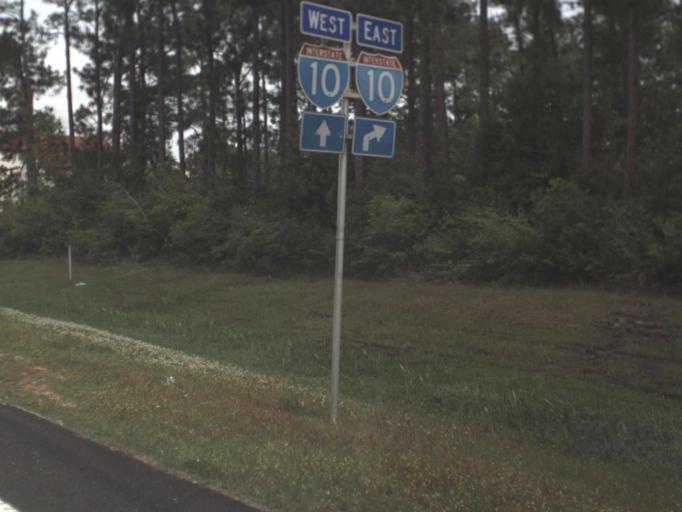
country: US
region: Florida
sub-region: Santa Rosa County
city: Bagdad
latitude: 30.5310
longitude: -87.0872
